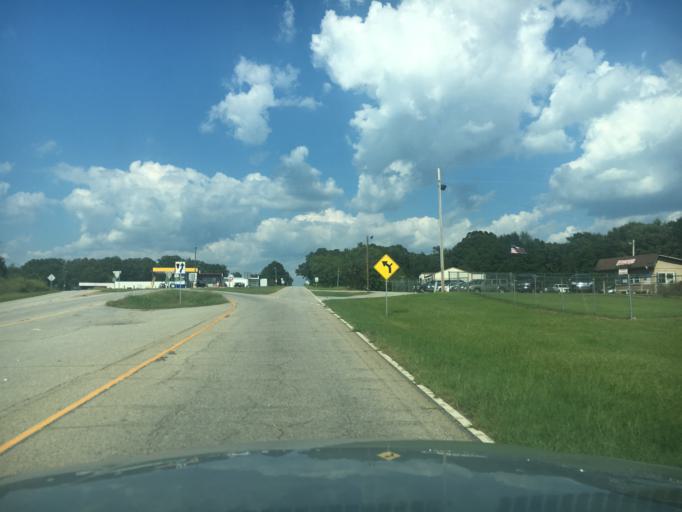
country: US
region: South Carolina
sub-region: Pickens County
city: Liberty
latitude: 34.7448
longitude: -82.6616
